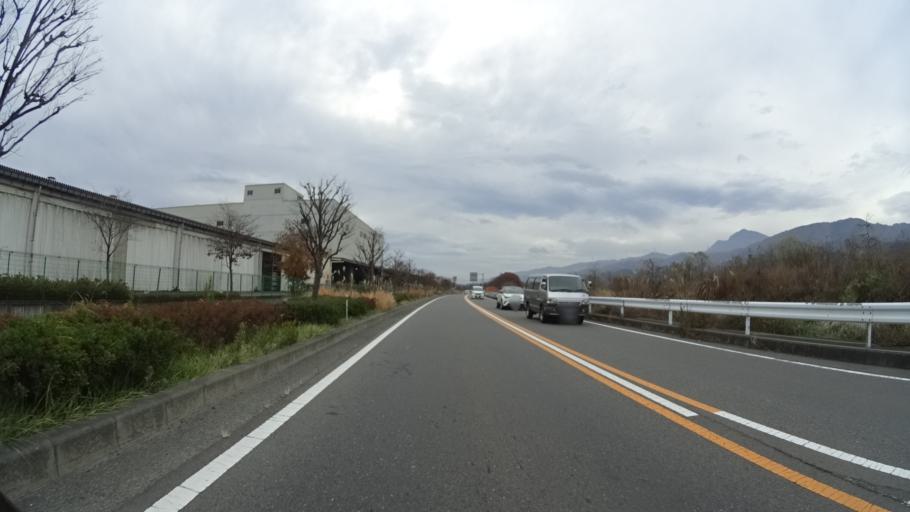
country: JP
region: Gunma
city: Numata
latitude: 36.6550
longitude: 139.0214
